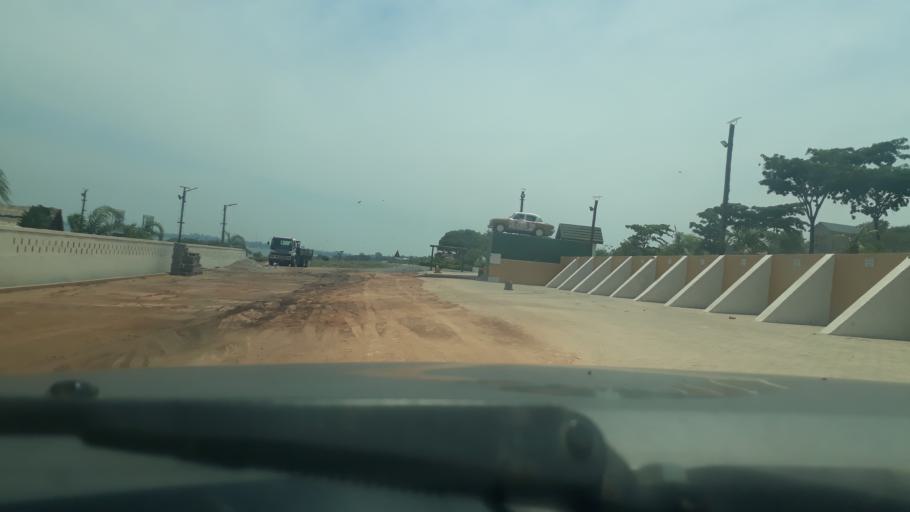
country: ZM
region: Luapula
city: Samfya
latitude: -11.3212
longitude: 29.5719
